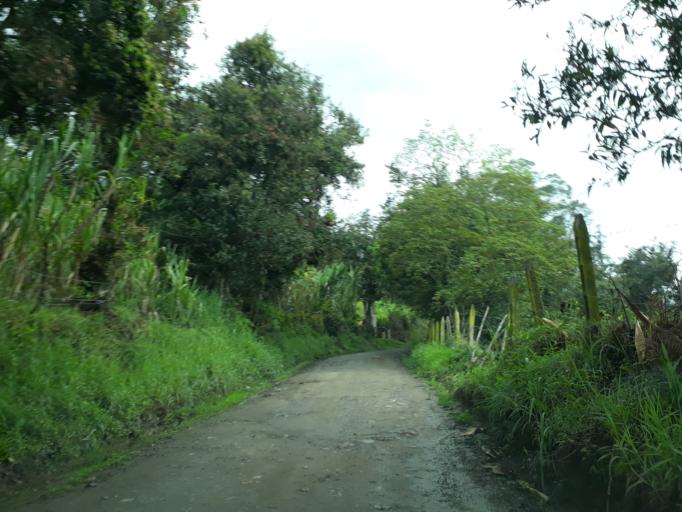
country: CO
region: Cundinamarca
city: Manta
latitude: 4.9907
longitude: -73.5580
